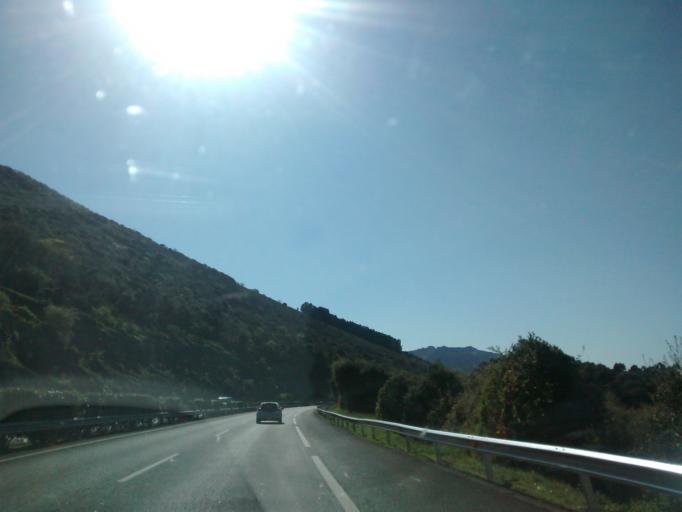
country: ES
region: Cantabria
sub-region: Provincia de Cantabria
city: Castro-Urdiales
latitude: 43.3980
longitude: -3.2711
